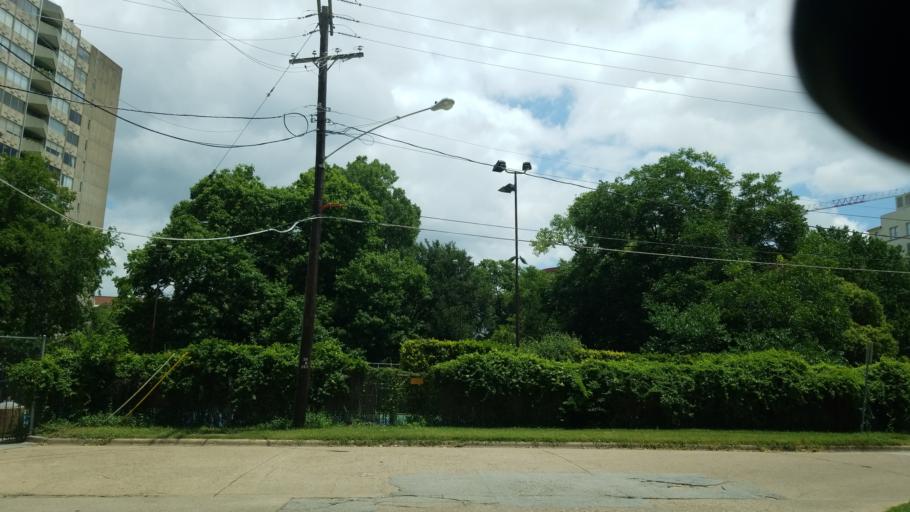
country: US
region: Texas
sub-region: Dallas County
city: Dallas
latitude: 32.7981
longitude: -96.8097
